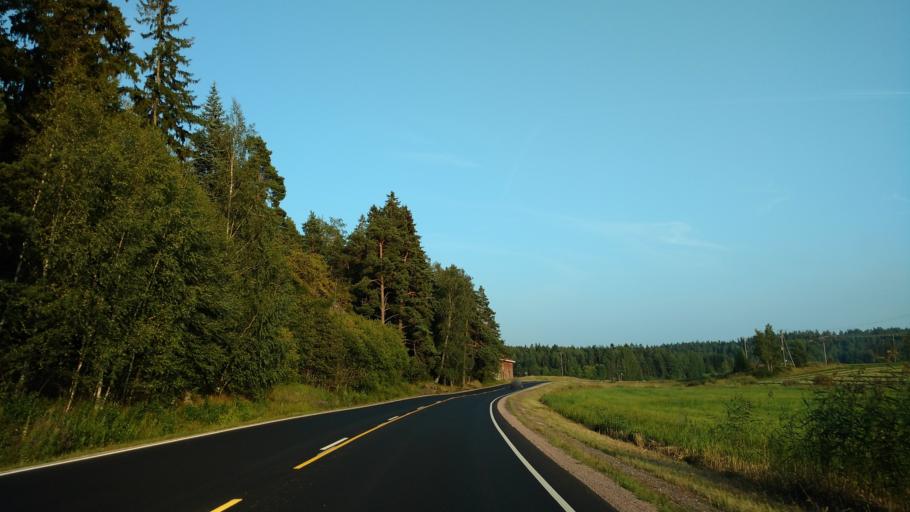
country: FI
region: Varsinais-Suomi
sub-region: Salo
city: Saerkisalo
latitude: 60.1852
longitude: 22.8941
